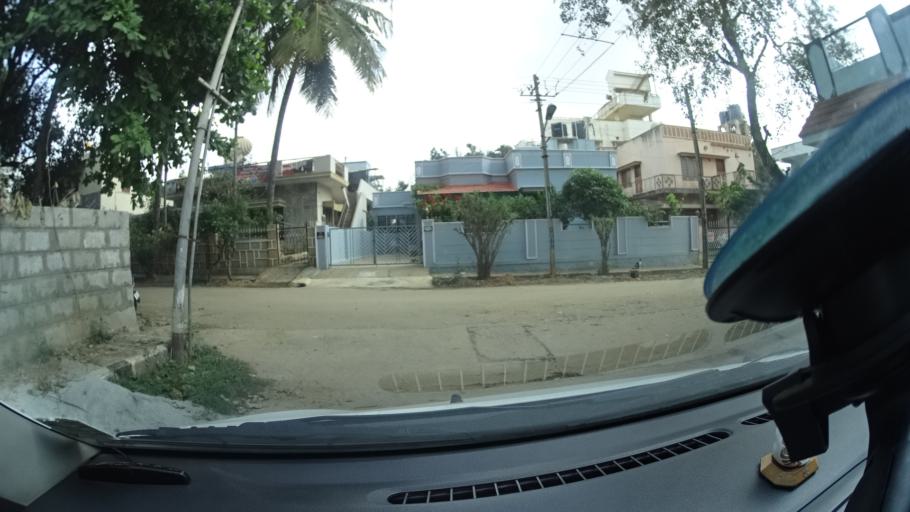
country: IN
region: Karnataka
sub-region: Bangalore Urban
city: Yelahanka
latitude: 13.0952
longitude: 77.5854
